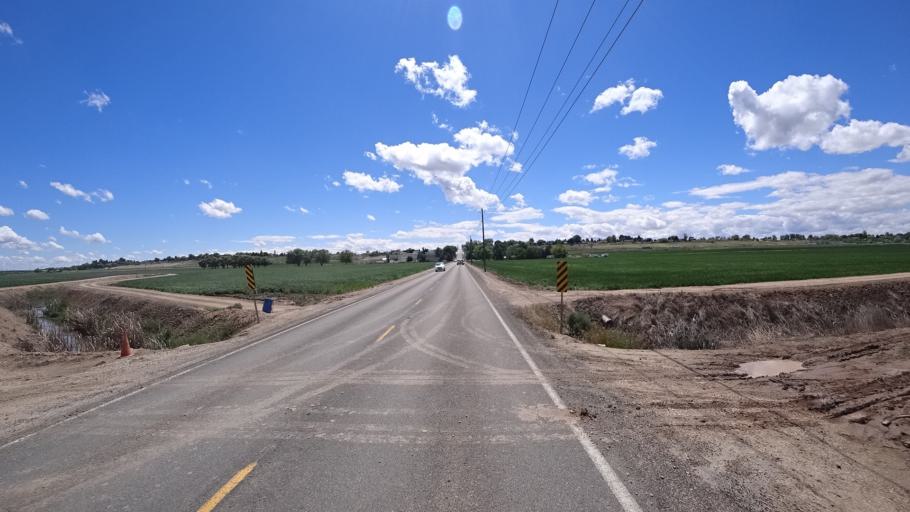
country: US
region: Idaho
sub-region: Ada County
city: Meridian
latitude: 43.6012
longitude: -116.4537
